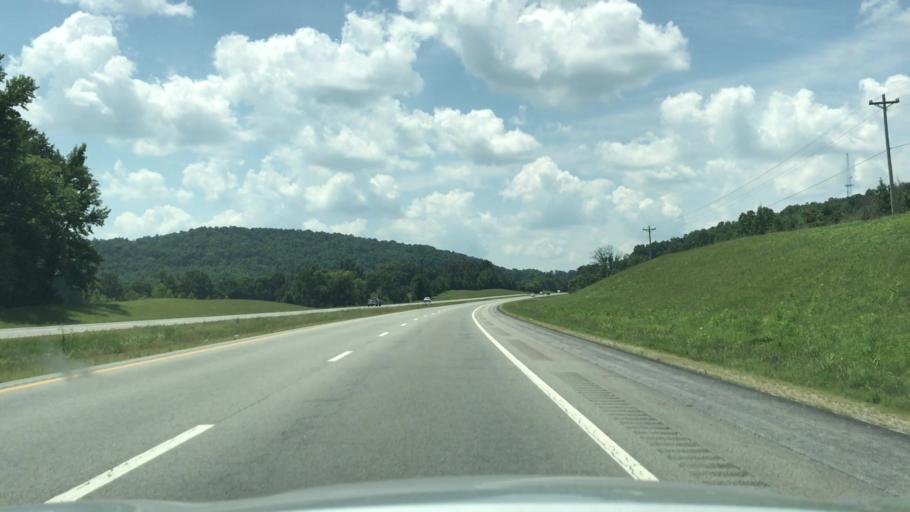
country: US
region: Tennessee
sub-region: Putnam County
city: Algood
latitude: 36.2177
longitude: -85.4161
